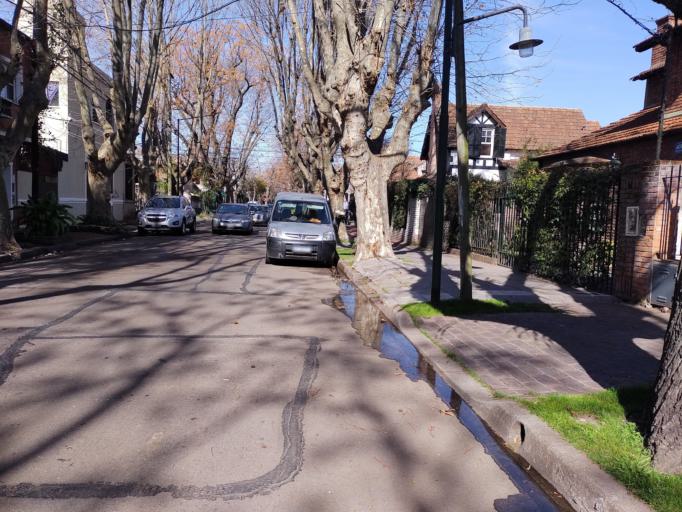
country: AR
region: Buenos Aires
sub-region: Partido de San Isidro
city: San Isidro
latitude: -34.4610
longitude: -58.5242
